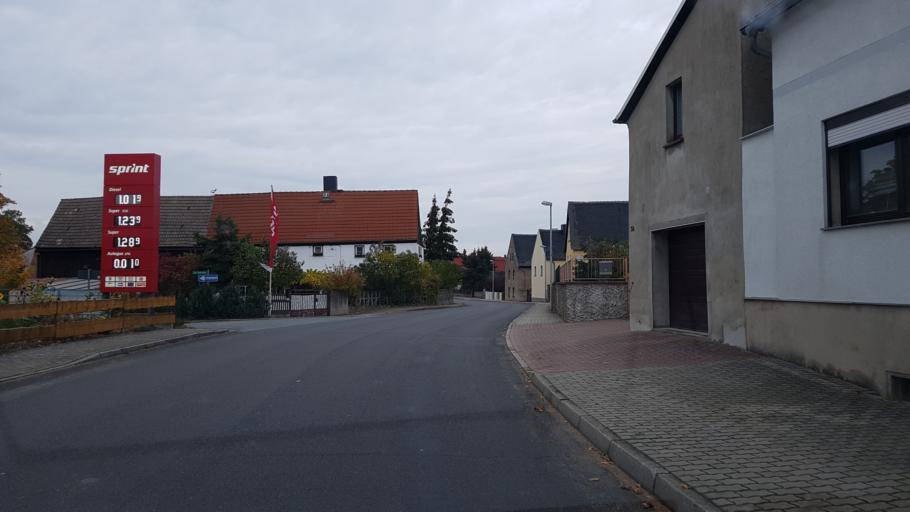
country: DE
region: Saxony
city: Falkenhain
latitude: 51.3935
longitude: 12.8771
